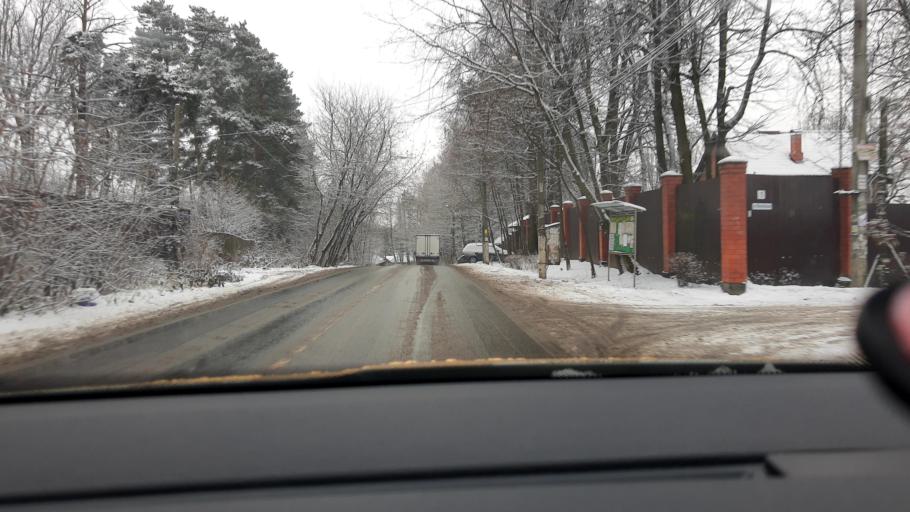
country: RU
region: Moskovskaya
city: Mamontovka
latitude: 55.9680
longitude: 37.8321
